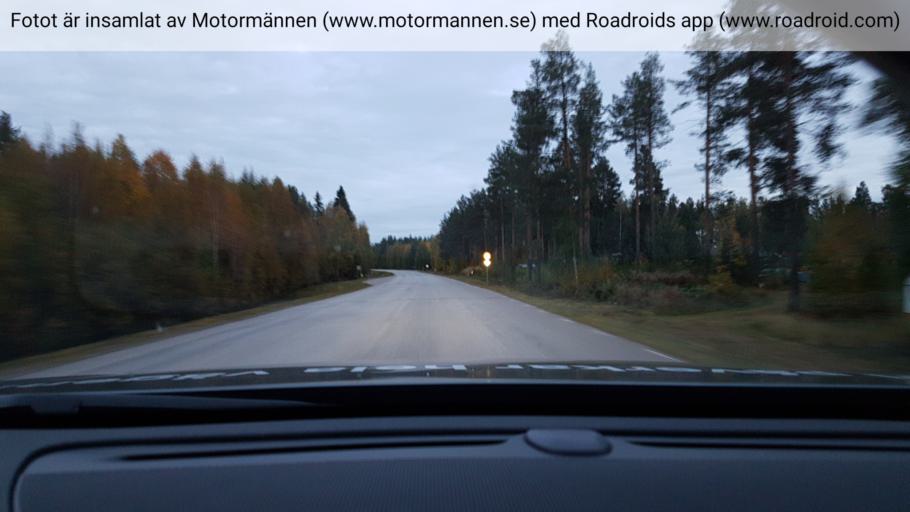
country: SE
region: Norrbotten
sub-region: Alvsbyns Kommun
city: AElvsbyn
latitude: 65.8369
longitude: 20.5172
